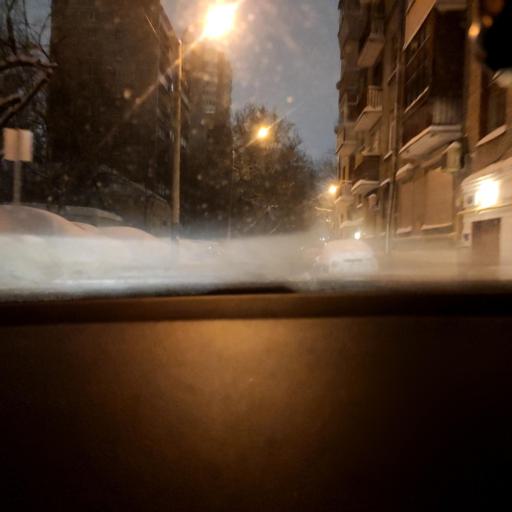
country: RU
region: Moscow
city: Vorob'yovo
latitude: 55.7253
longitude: 37.5246
